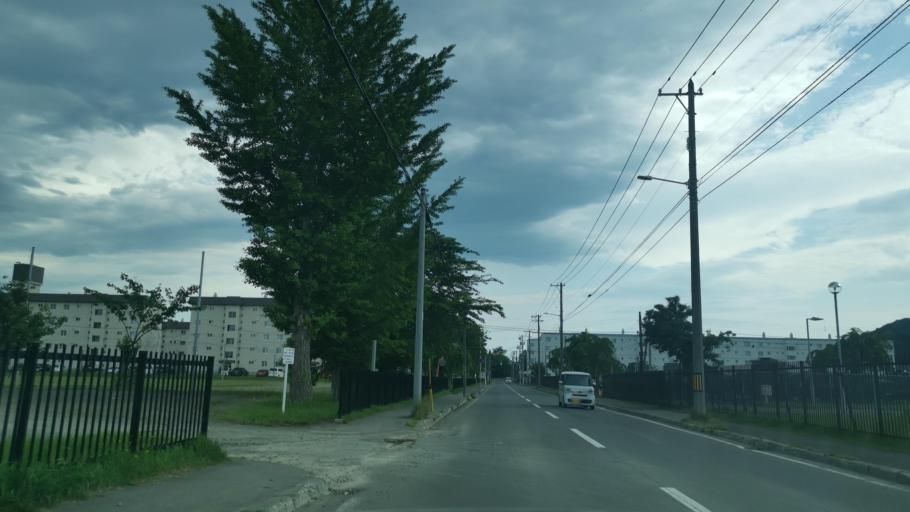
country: JP
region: Hokkaido
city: Sapporo
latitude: 43.0243
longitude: 141.3492
